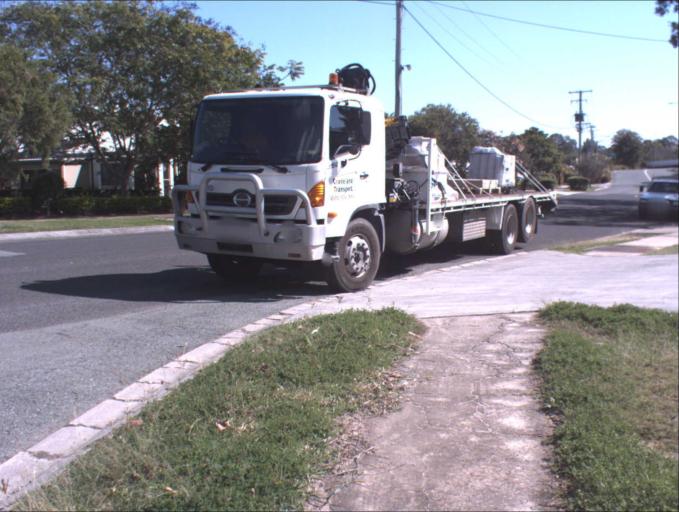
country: AU
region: Queensland
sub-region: Logan
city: Waterford West
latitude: -27.6981
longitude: 153.1542
